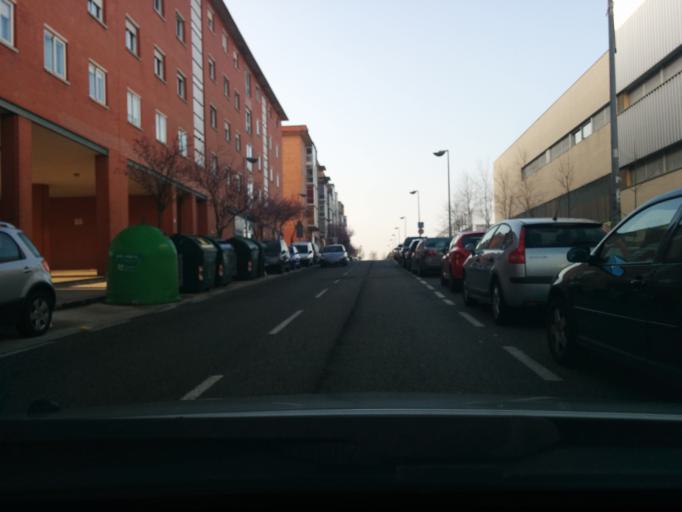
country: ES
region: Navarre
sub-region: Provincia de Navarra
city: Burlata
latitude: 42.8108
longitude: -1.6196
